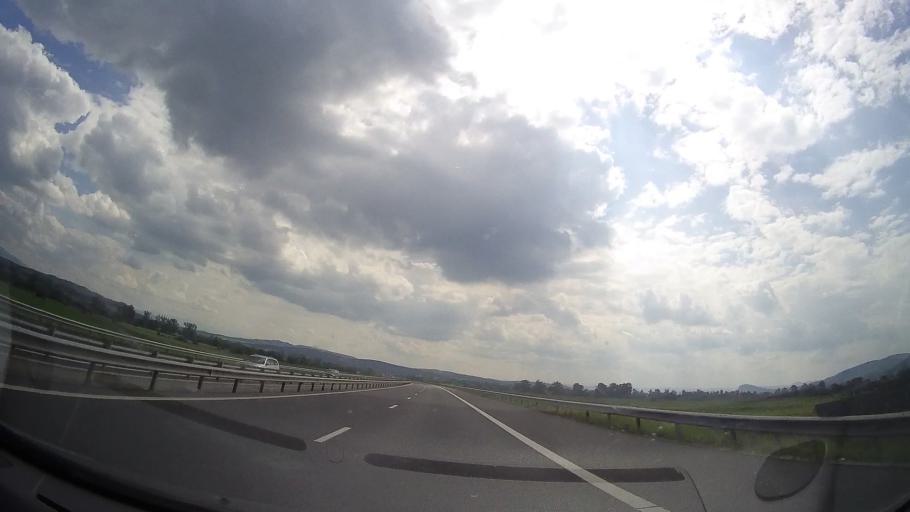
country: RO
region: Hunedoara
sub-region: Comuna Turdas
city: Pricaz
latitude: 45.8692
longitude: 23.1594
